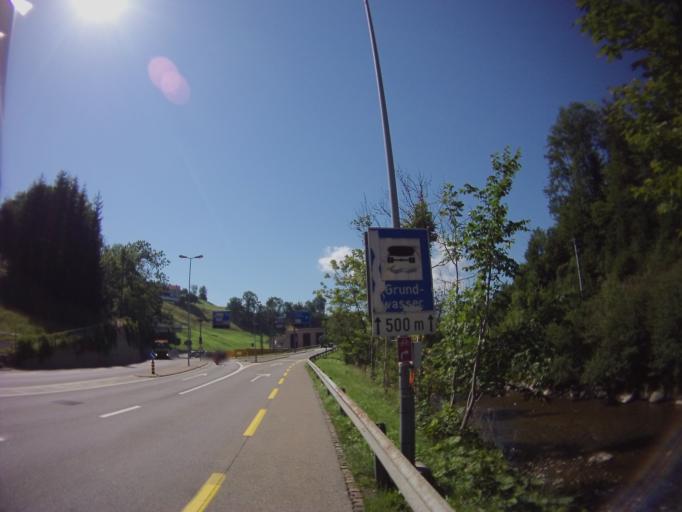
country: CH
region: Schwyz
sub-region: Bezirk Einsiedeln
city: Einsiedeln
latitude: 47.1477
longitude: 8.7505
